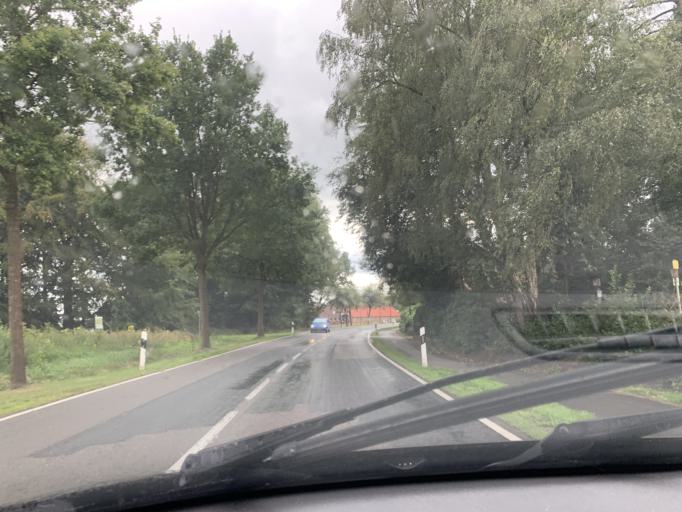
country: DE
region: Lower Saxony
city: Wiefelstede
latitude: 53.3029
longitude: 8.0584
